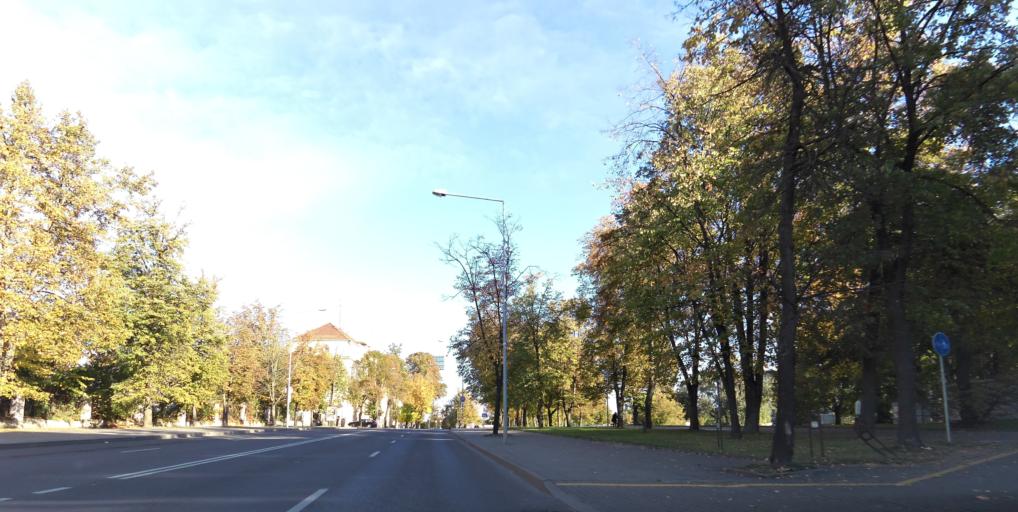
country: LT
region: Vilnius County
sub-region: Vilnius
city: Vilnius
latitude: 54.6903
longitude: 25.2887
